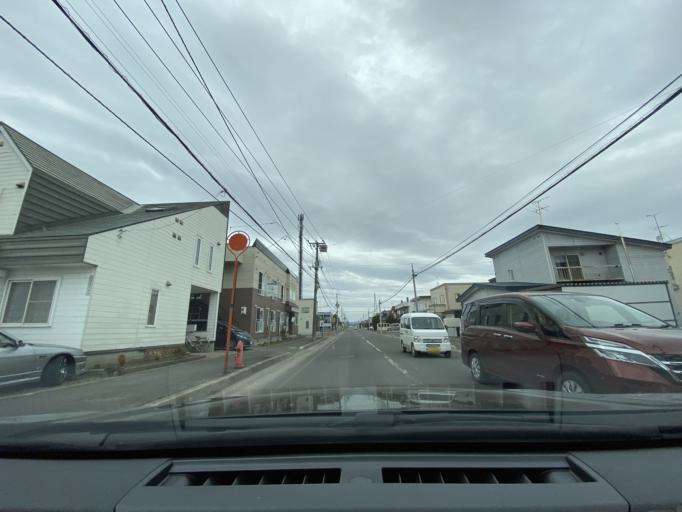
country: JP
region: Hokkaido
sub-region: Asahikawa-shi
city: Asahikawa
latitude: 43.7857
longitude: 142.4178
